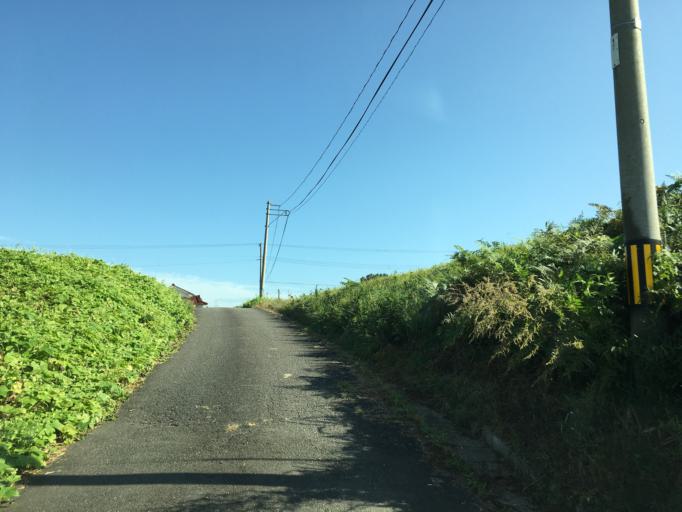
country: JP
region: Fukushima
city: Motomiya
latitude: 37.5433
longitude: 140.3733
